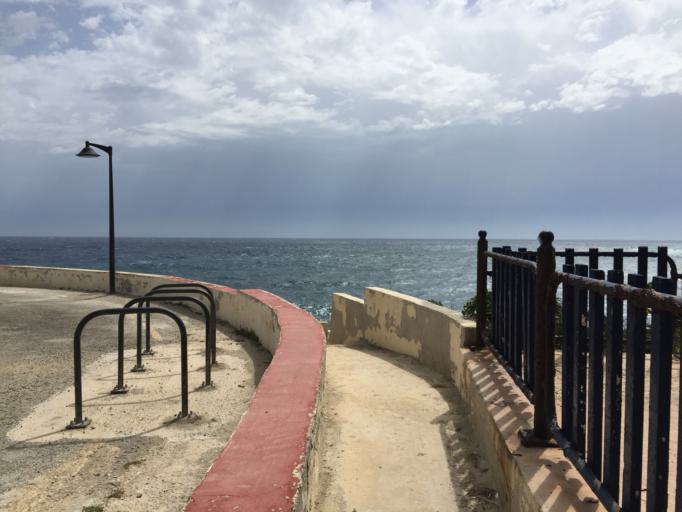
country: MT
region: Iz-Zebbug
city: Zebbug
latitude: 36.0756
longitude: 14.2578
